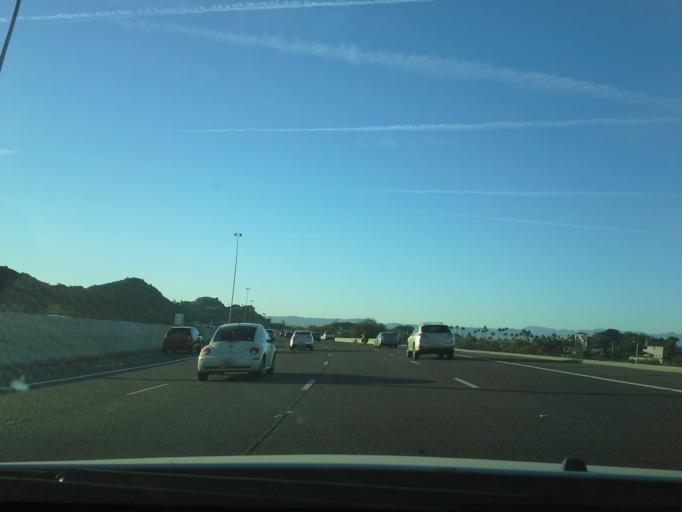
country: US
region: Arizona
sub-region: Maricopa County
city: Paradise Valley
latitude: 33.5606
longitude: -112.0384
